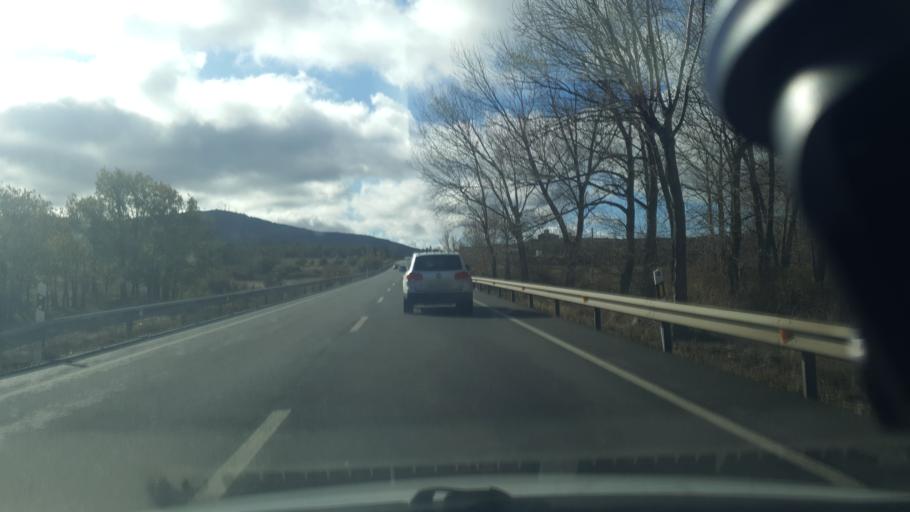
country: ES
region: Castille and Leon
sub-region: Provincia de Segovia
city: Villacastin
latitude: 40.7514
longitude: -4.4546
